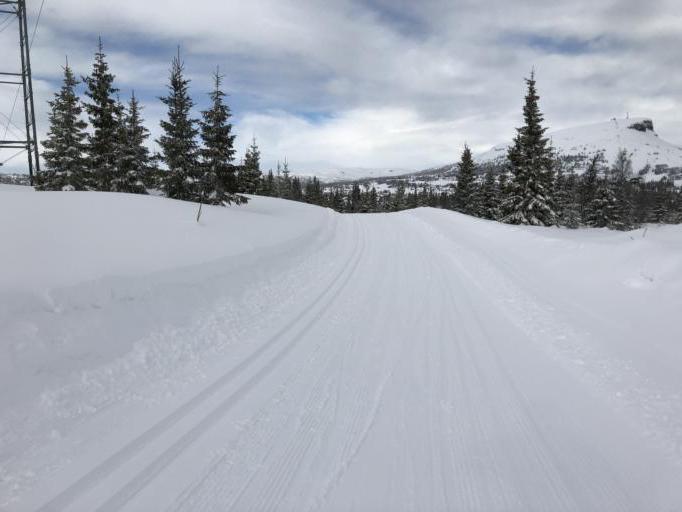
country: NO
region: Oppland
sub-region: Gausdal
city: Segalstad bru
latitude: 61.3225
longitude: 10.0810
